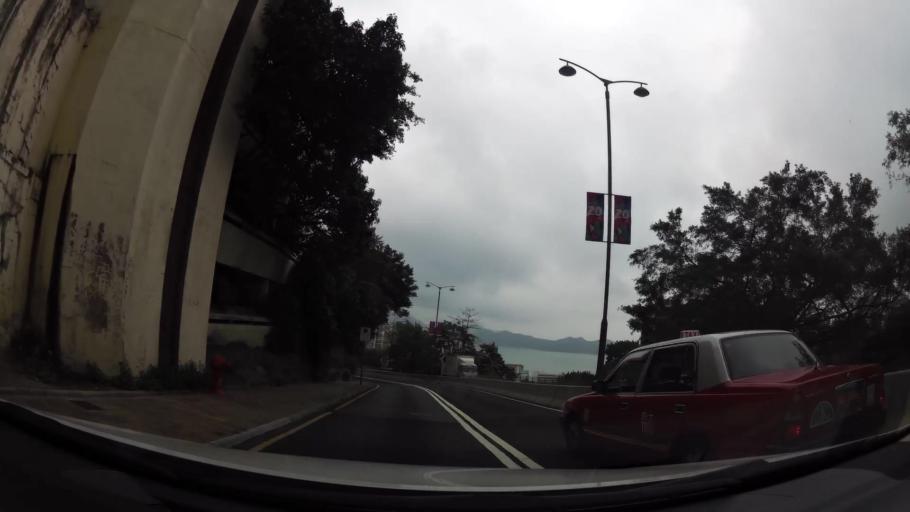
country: HK
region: Central and Western
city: Central
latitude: 22.2581
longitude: 114.1367
